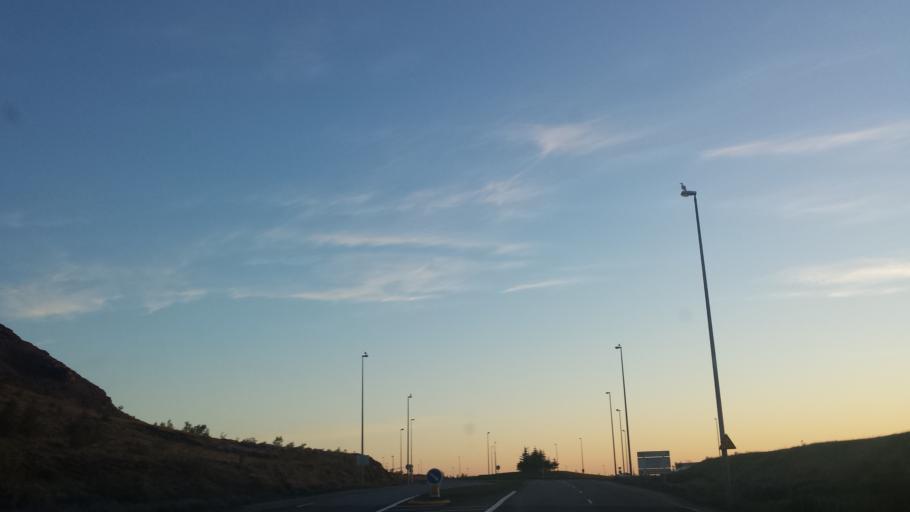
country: IS
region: Capital Region
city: Mosfellsbaer
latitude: 64.1646
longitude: -21.7022
